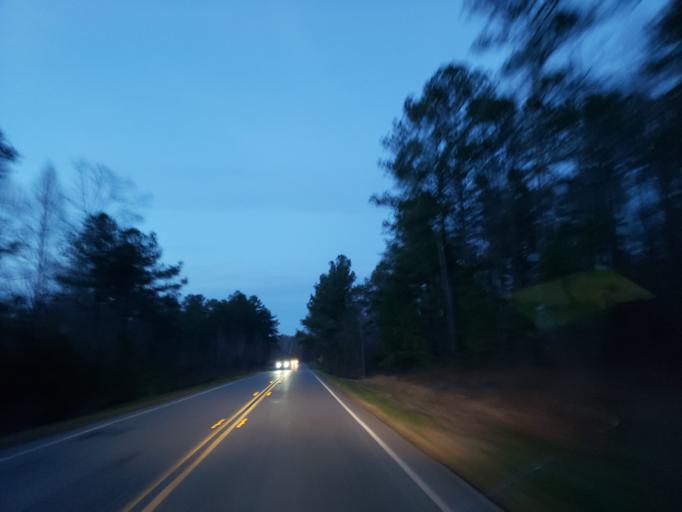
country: US
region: Georgia
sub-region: Cherokee County
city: Ball Ground
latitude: 34.3102
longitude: -84.2697
